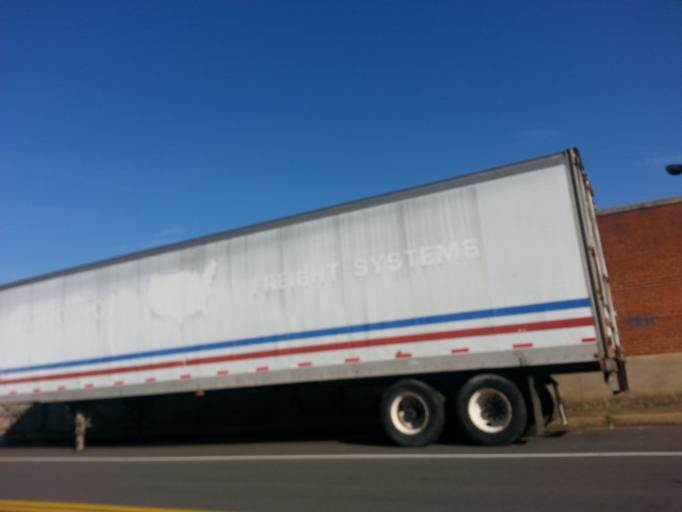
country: US
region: Tennessee
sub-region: Knox County
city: Knoxville
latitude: 35.9719
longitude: -83.9139
